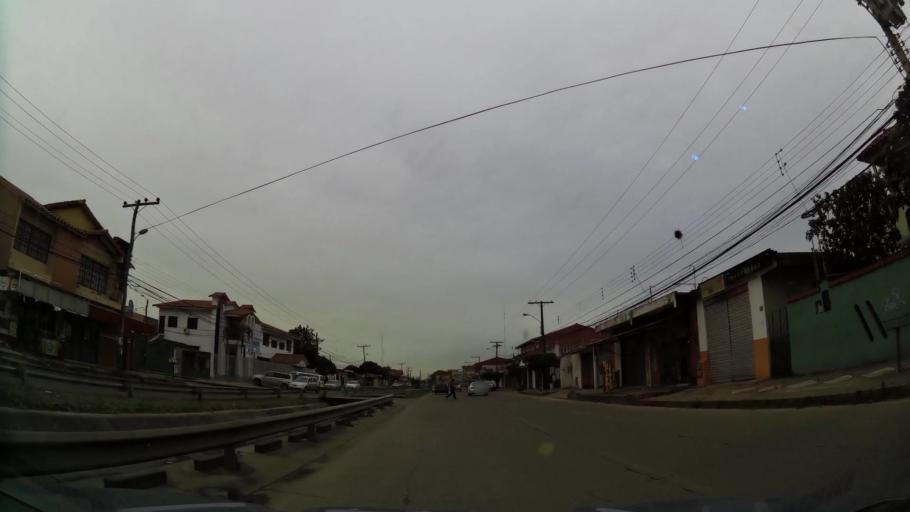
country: BO
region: Santa Cruz
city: Santa Cruz de la Sierra
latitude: -17.8164
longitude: -63.1771
